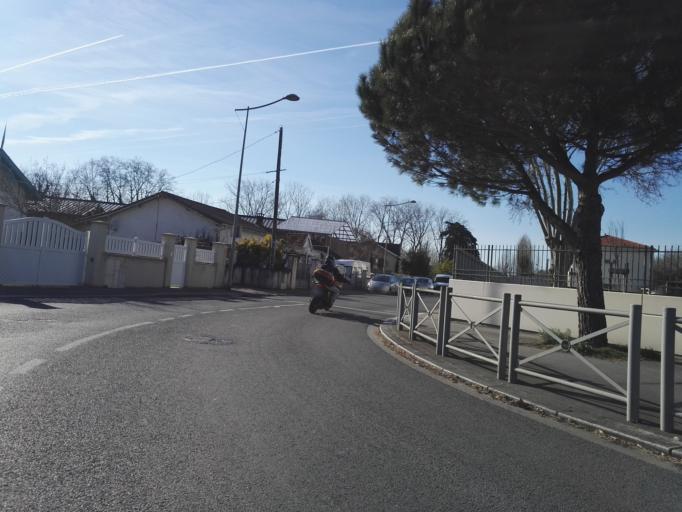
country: FR
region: Aquitaine
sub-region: Departement de la Gironde
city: Merignac
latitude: 44.8268
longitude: -0.6266
